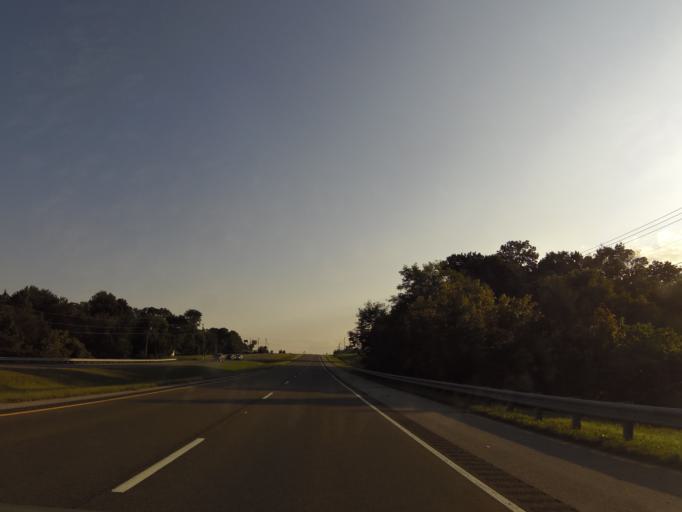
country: US
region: Tennessee
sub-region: Knox County
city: Mascot
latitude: 36.0787
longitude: -83.7680
